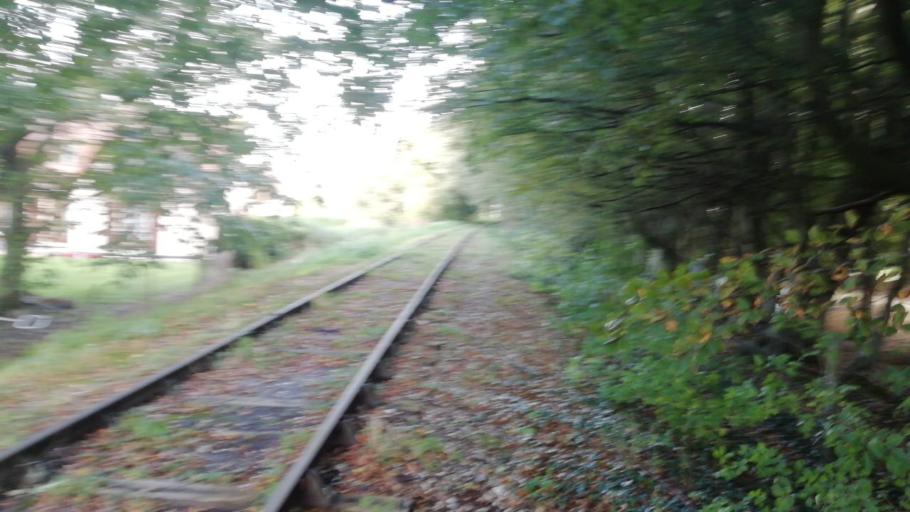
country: FR
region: Haute-Normandie
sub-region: Departement de la Seine-Maritime
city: Gonneville-la-Mallet
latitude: 49.6382
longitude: 0.2596
